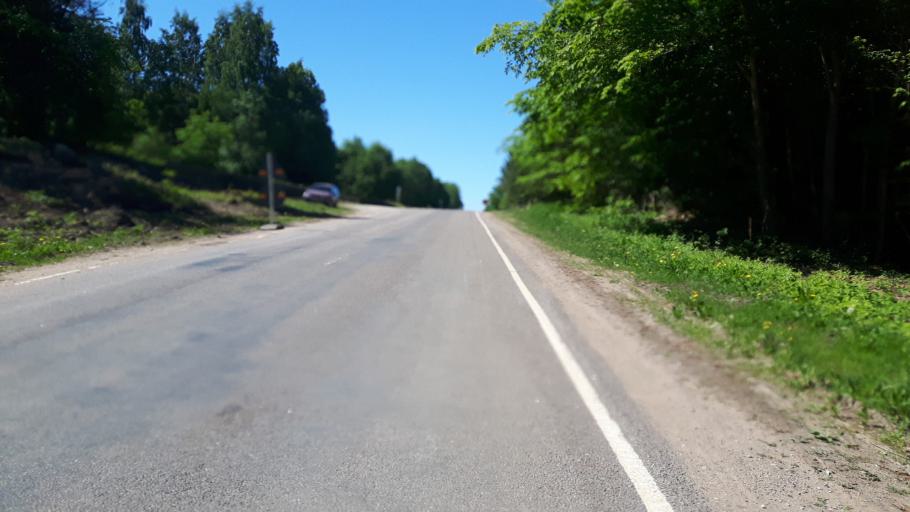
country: EE
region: Ida-Virumaa
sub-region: Narva-Joesuu linn
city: Narva-Joesuu
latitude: 59.4138
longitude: 27.9576
